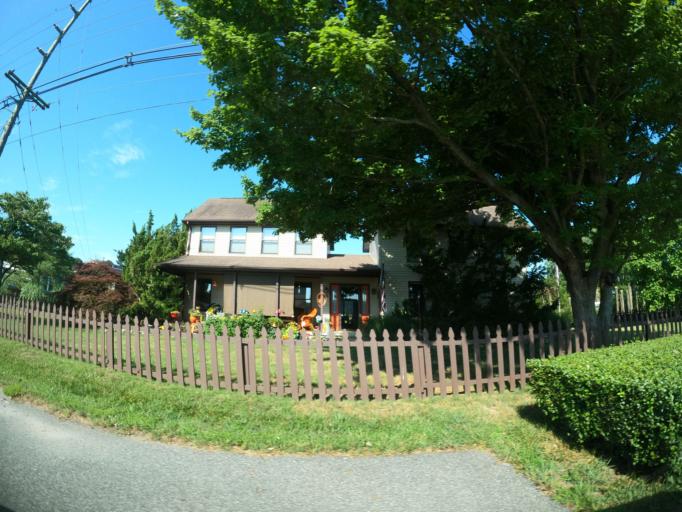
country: US
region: Delaware
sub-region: Sussex County
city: Ocean View
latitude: 38.4821
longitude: -75.1187
